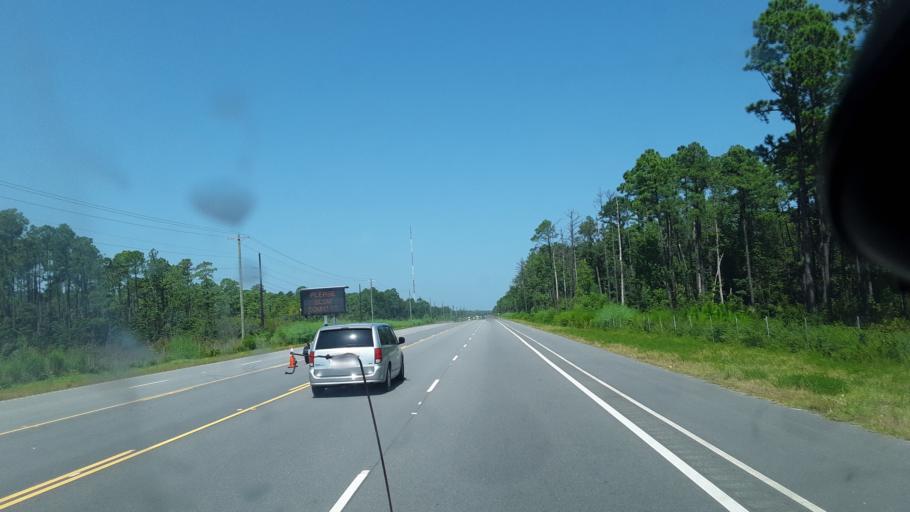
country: US
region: South Carolina
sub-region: Horry County
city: Myrtle Beach
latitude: 33.7736
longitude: -78.8701
